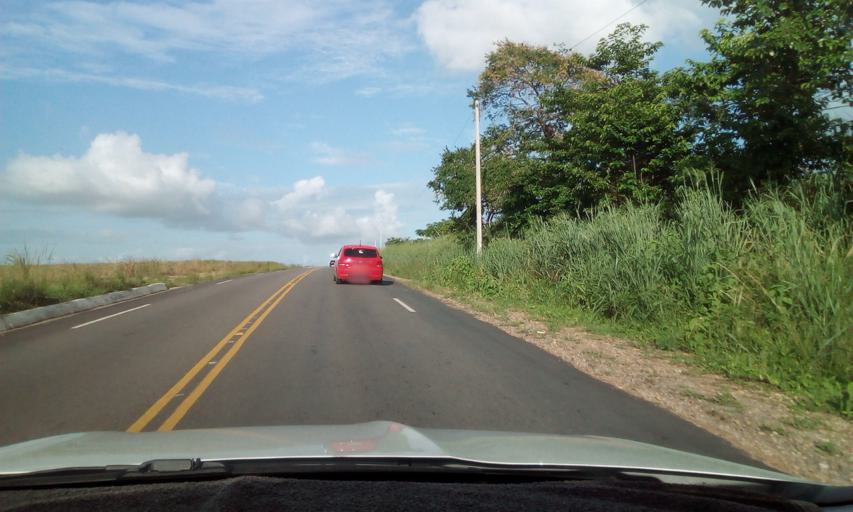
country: BR
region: Paraiba
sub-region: Mamanguape
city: Mamanguape
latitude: -6.8112
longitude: -35.1875
